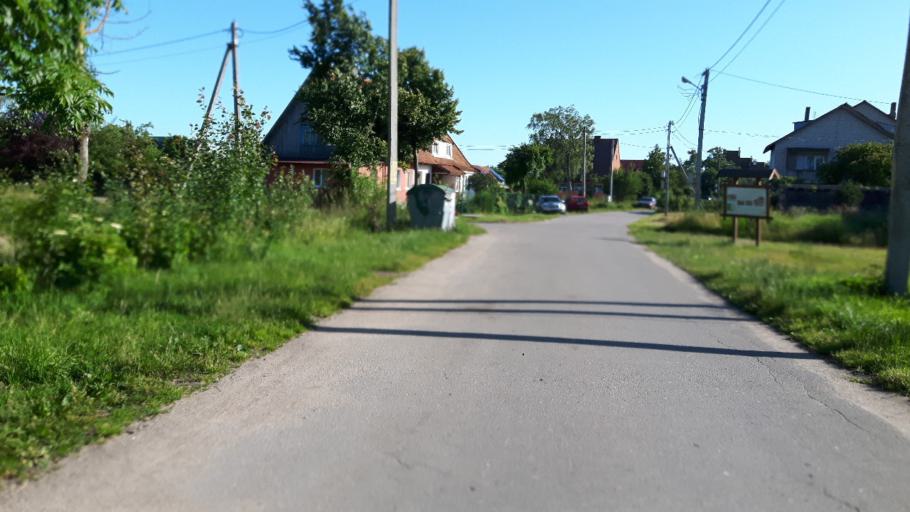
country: LT
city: Nida
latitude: 55.1523
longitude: 20.8551
